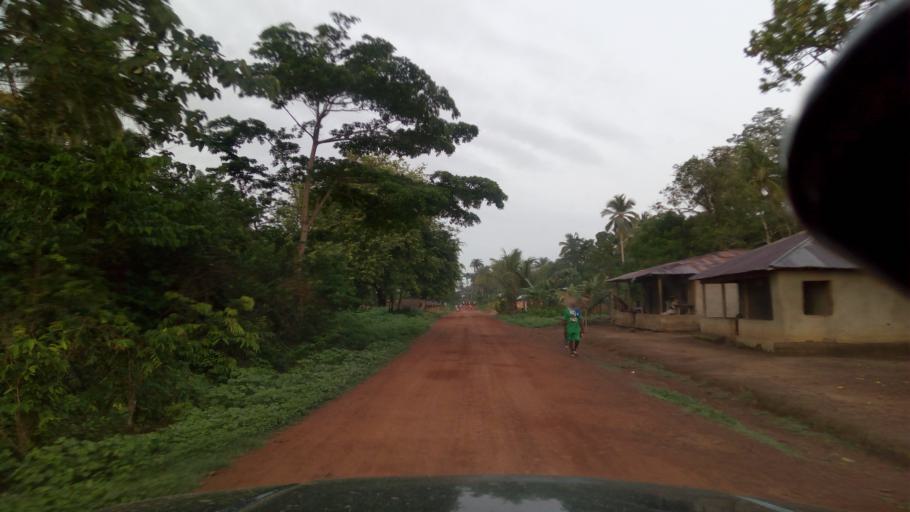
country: SL
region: Northern Province
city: Port Loko
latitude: 8.7407
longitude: -12.7942
